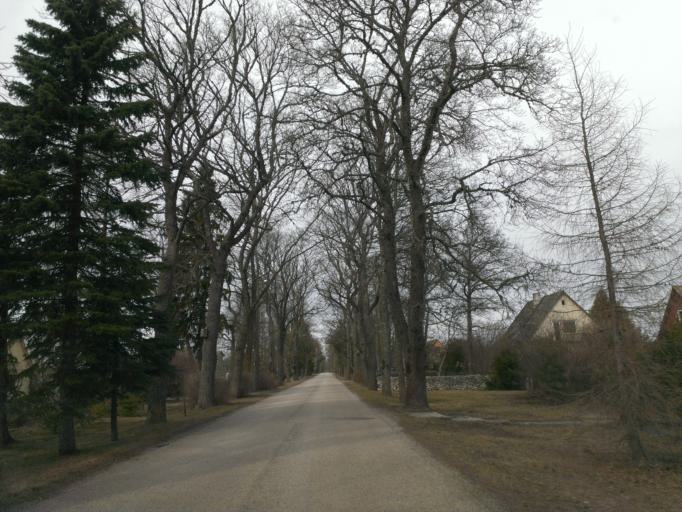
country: EE
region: Laeaene
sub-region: Lihula vald
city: Lihula
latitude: 58.5827
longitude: 23.5371
